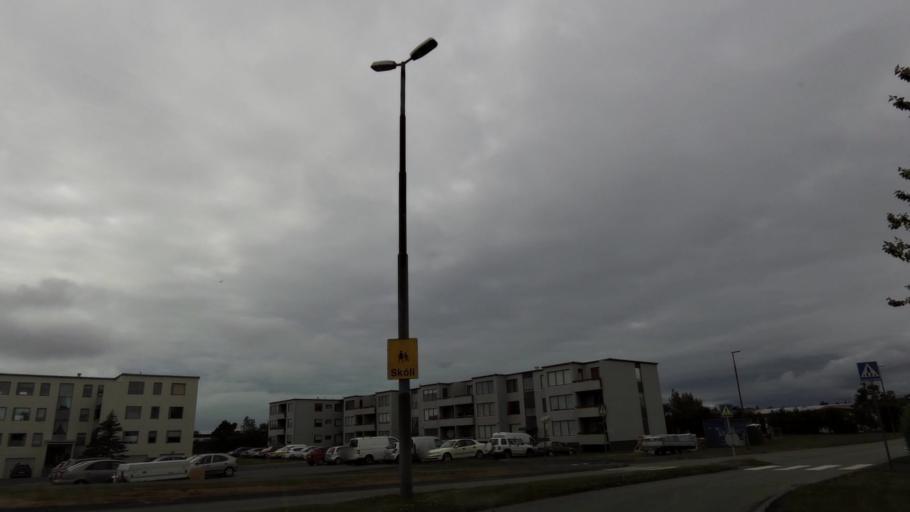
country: IS
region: Capital Region
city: Hafnarfjoerdur
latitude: 64.0799
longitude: -21.9617
